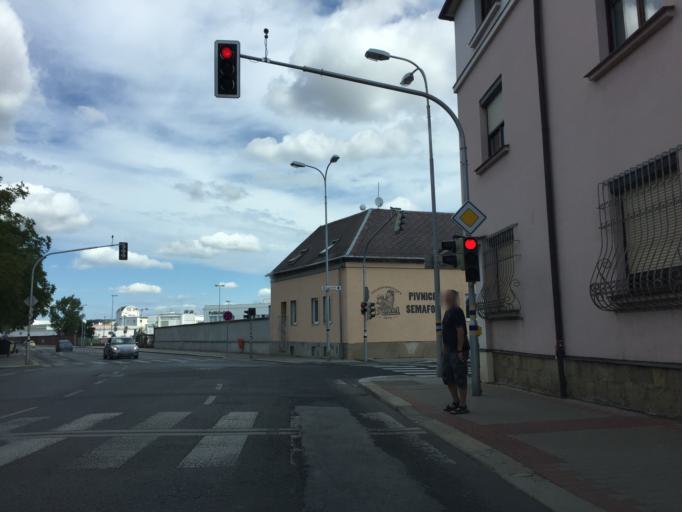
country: CZ
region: Central Bohemia
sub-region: Okres Mlada Boleslav
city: Mlada Boleslav
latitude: 50.4143
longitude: 14.9187
